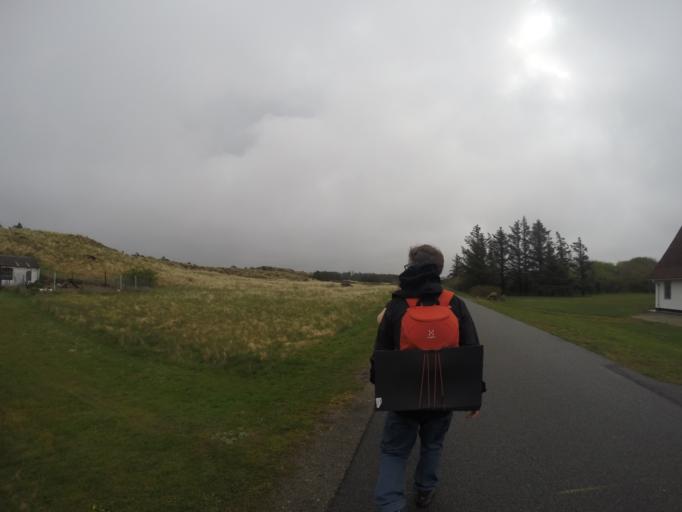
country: DK
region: North Denmark
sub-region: Thisted Kommune
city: Hanstholm
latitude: 57.0363
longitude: 8.5239
